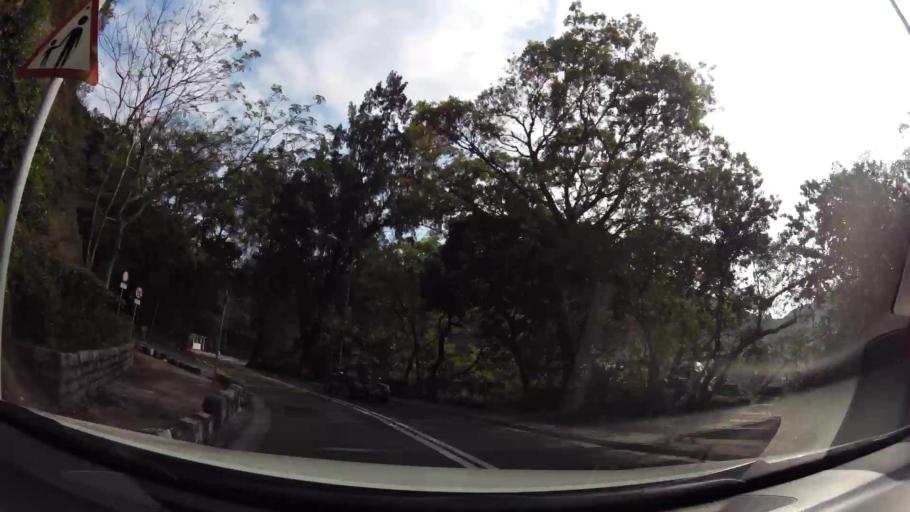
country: HK
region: Wanchai
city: Wan Chai
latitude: 22.2665
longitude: 114.1906
